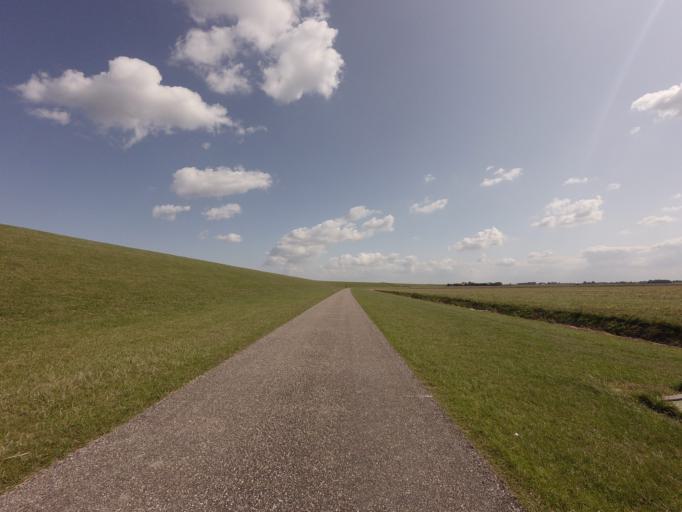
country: NL
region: Friesland
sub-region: Gemeente Ferwerderadiel
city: Hallum
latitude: 53.3244
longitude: 5.7253
